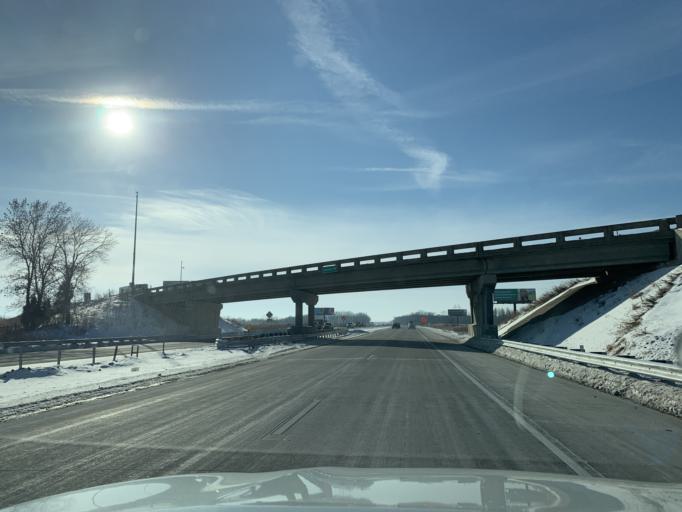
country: US
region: Minnesota
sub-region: Anoka County
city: Columbus
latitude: 45.2153
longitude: -93.0339
